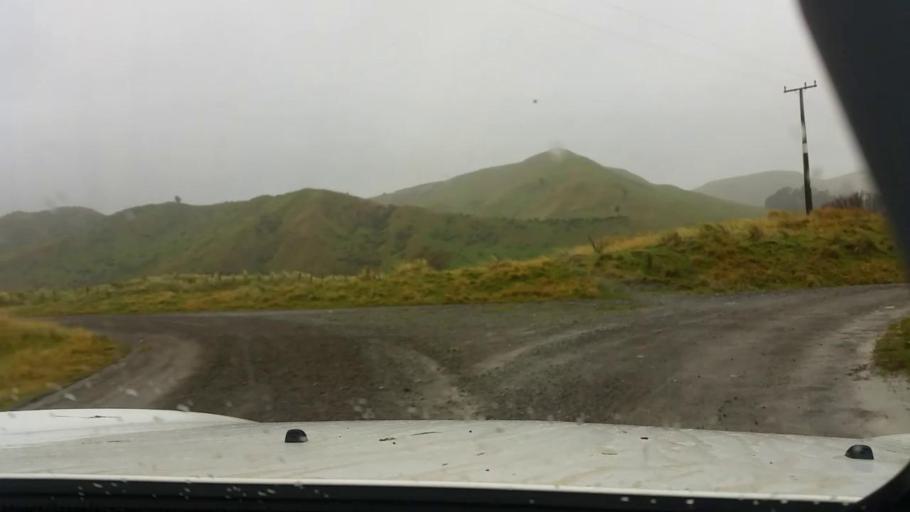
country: NZ
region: Wellington
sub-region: Masterton District
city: Masterton
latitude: -41.2521
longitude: 175.9156
